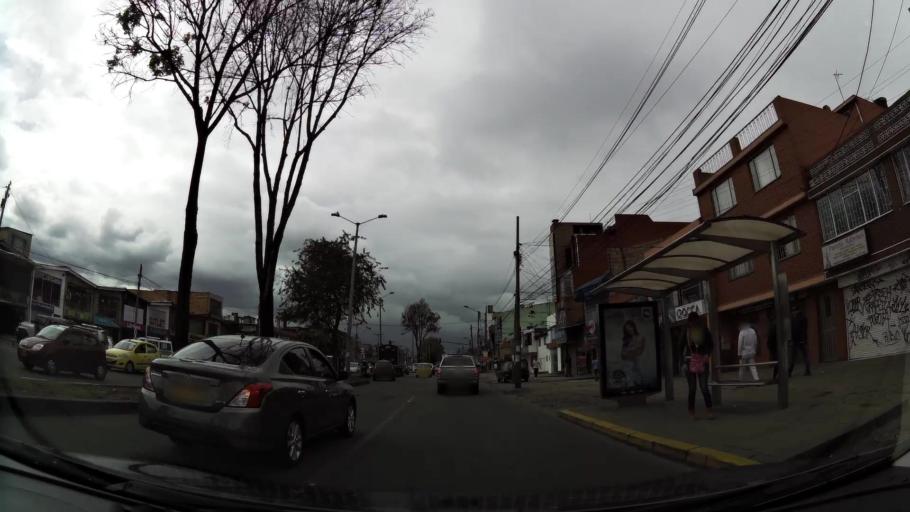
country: CO
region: Bogota D.C.
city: Barrio San Luis
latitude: 4.6907
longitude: -74.0993
